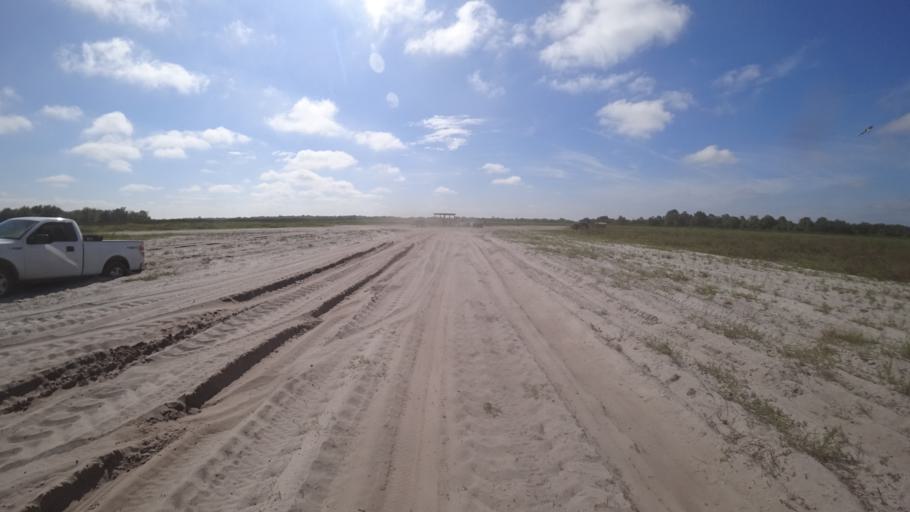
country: US
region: Florida
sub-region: DeSoto County
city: Arcadia
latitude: 27.2894
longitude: -82.0784
